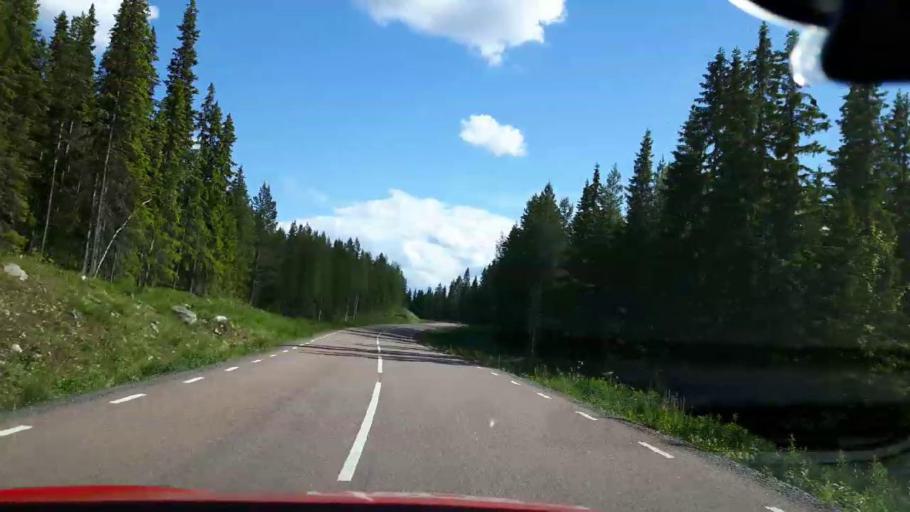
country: SE
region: Jaemtland
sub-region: Krokoms Kommun
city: Valla
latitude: 64.0630
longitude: 14.1505
